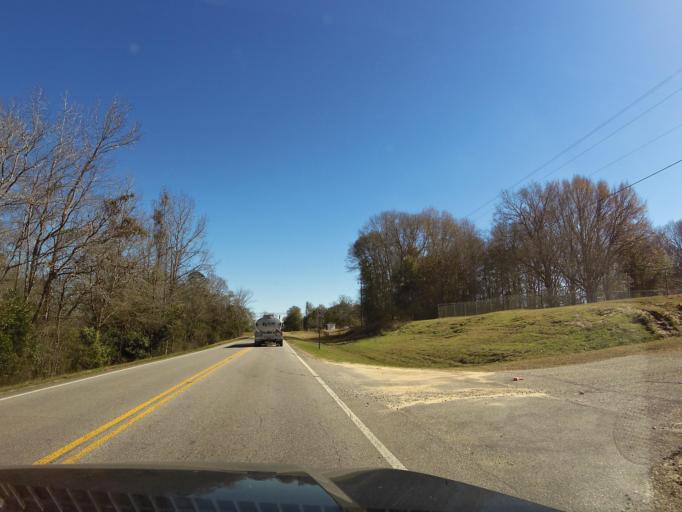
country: US
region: Alabama
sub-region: Bullock County
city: Union Springs
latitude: 32.0807
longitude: -85.5310
